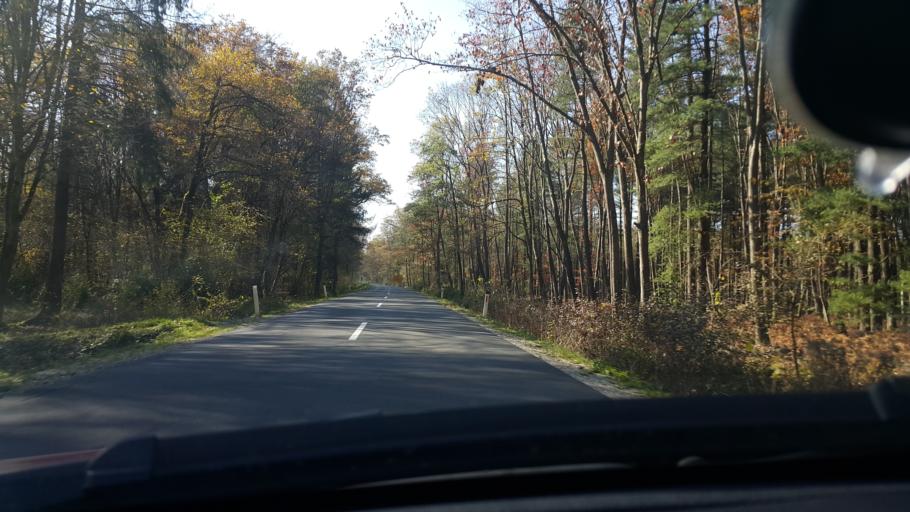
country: SI
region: Brezice
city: Brezice
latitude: 45.9427
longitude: 15.6576
